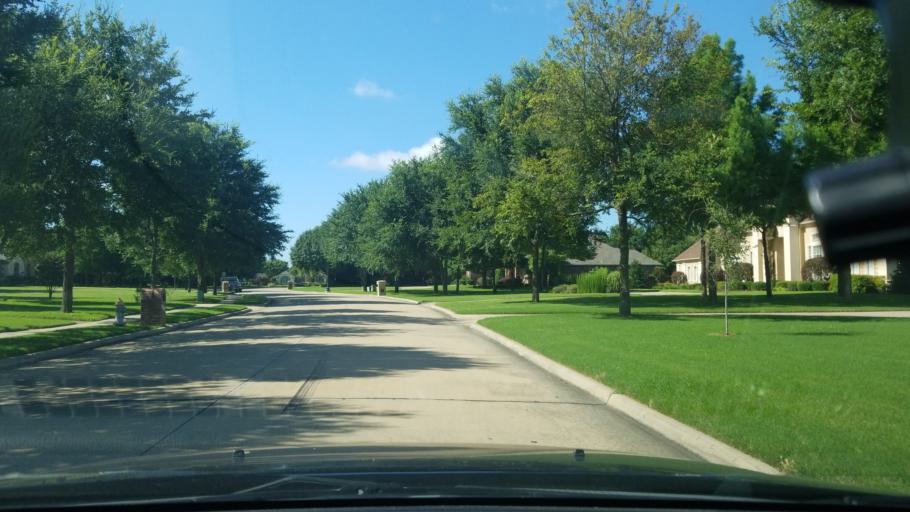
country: US
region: Texas
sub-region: Dallas County
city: Sunnyvale
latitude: 32.8095
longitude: -96.5869
